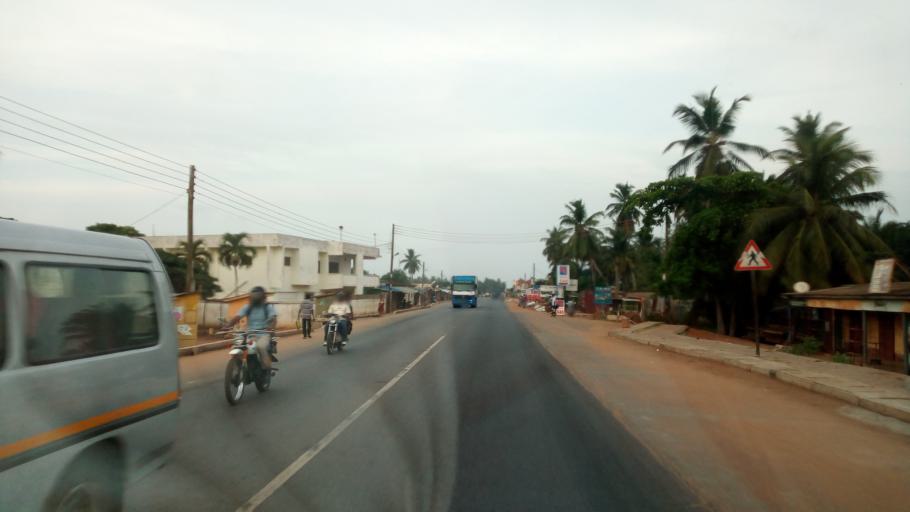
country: TG
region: Maritime
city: Lome
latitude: 6.1167
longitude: 1.1727
